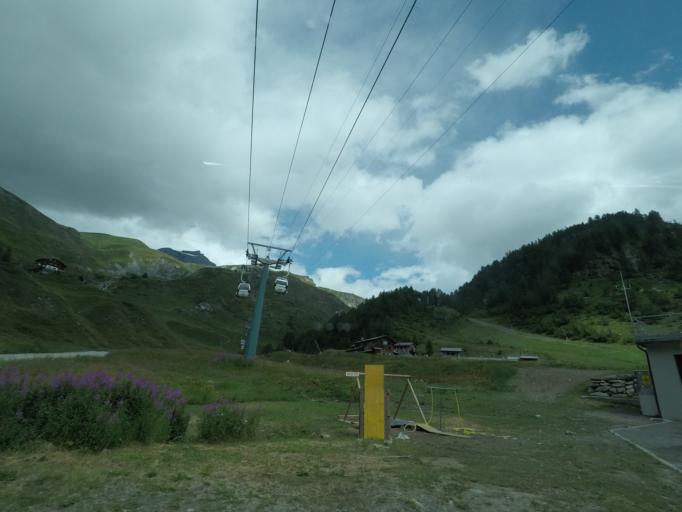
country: IT
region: Aosta Valley
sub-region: Valle d'Aosta
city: Paquier
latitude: 45.9351
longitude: 7.6363
